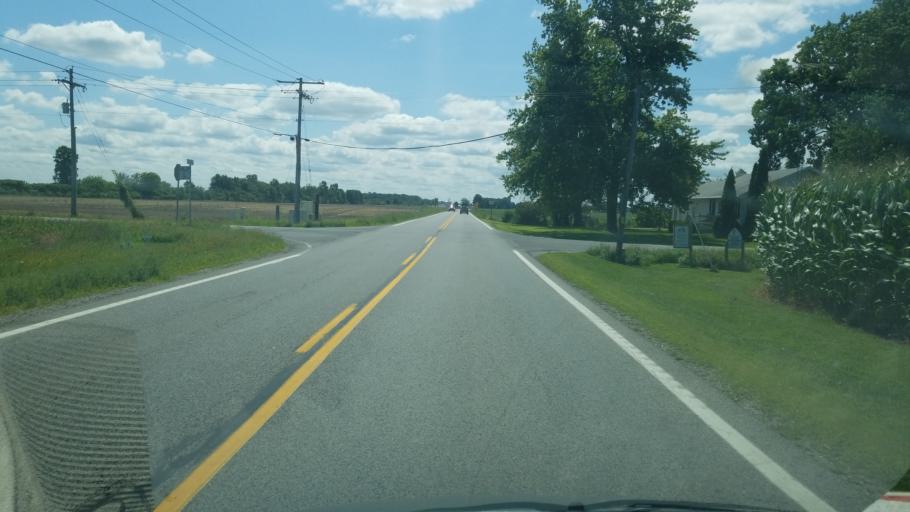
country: US
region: Ohio
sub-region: Fulton County
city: Delta
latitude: 41.6278
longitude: -84.0346
